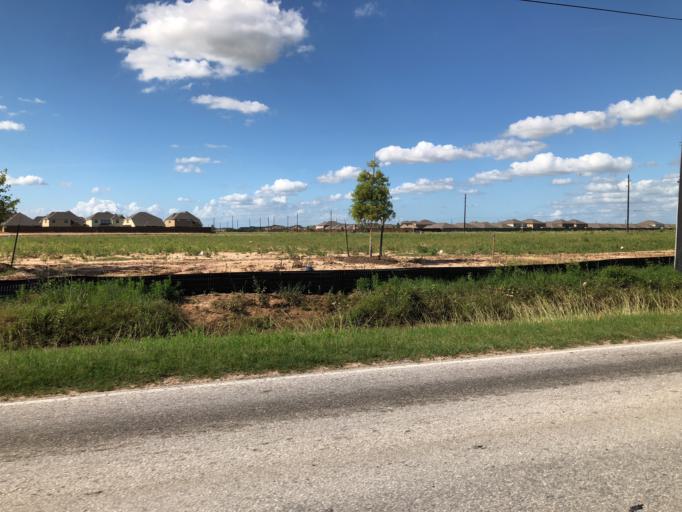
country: US
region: Texas
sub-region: Harris County
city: Katy
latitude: 29.8315
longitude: -95.7913
